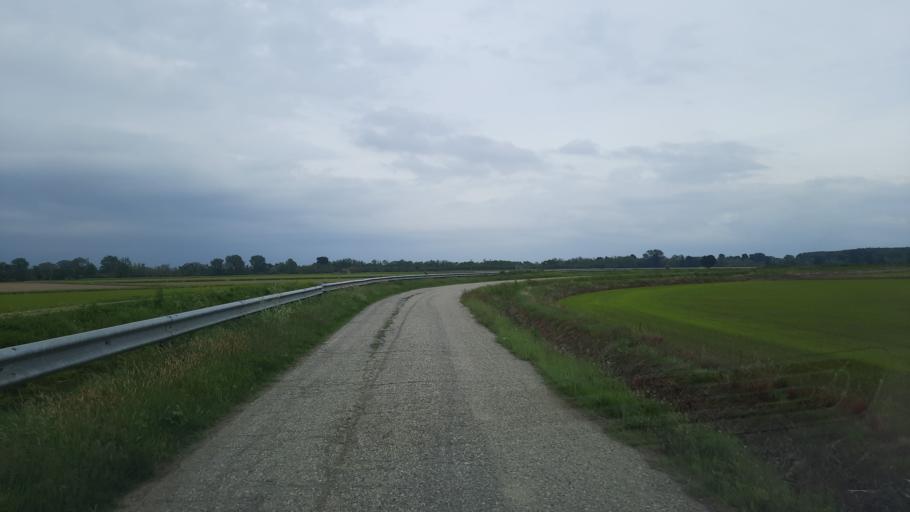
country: IT
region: Lombardy
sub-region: Provincia di Pavia
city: Cozzo
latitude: 45.2183
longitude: 8.6084
